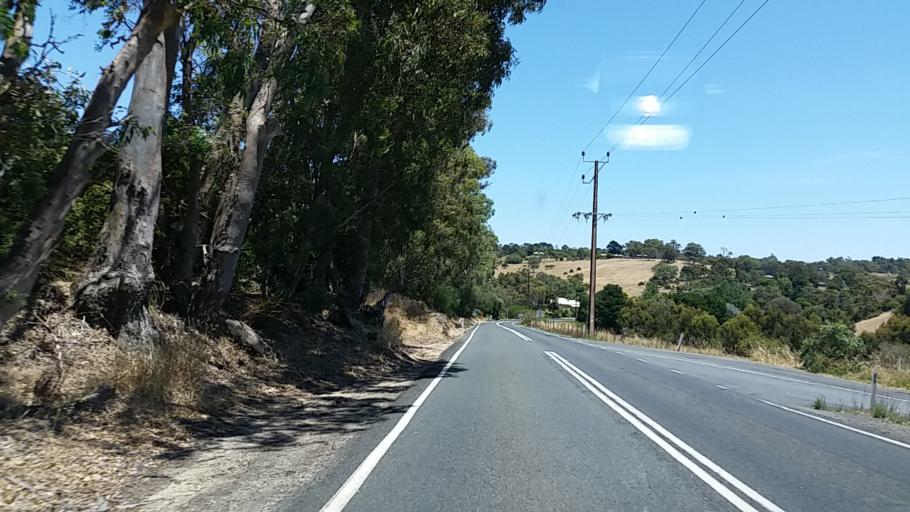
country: AU
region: South Australia
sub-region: Tea Tree Gully
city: Golden Grove
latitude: -34.8236
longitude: 138.7831
